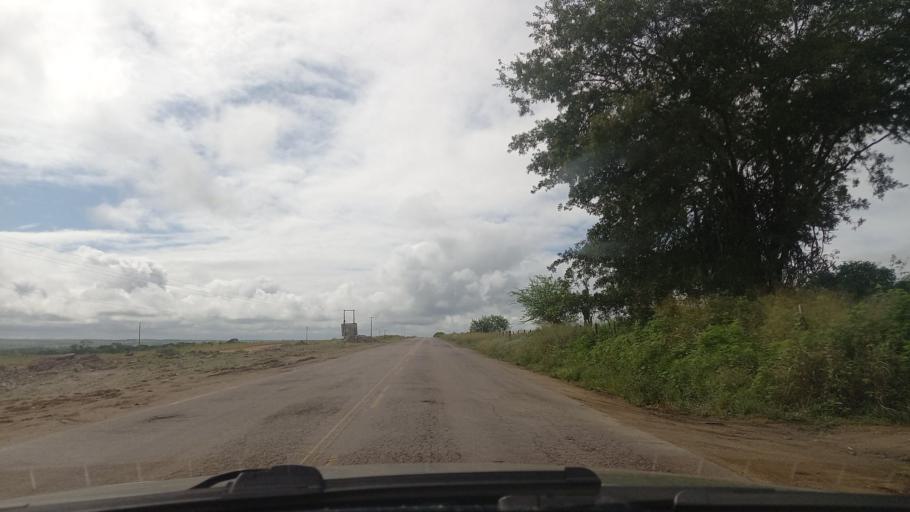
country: BR
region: Alagoas
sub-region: Batalha
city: Batalha
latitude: -9.6649
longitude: -37.1612
